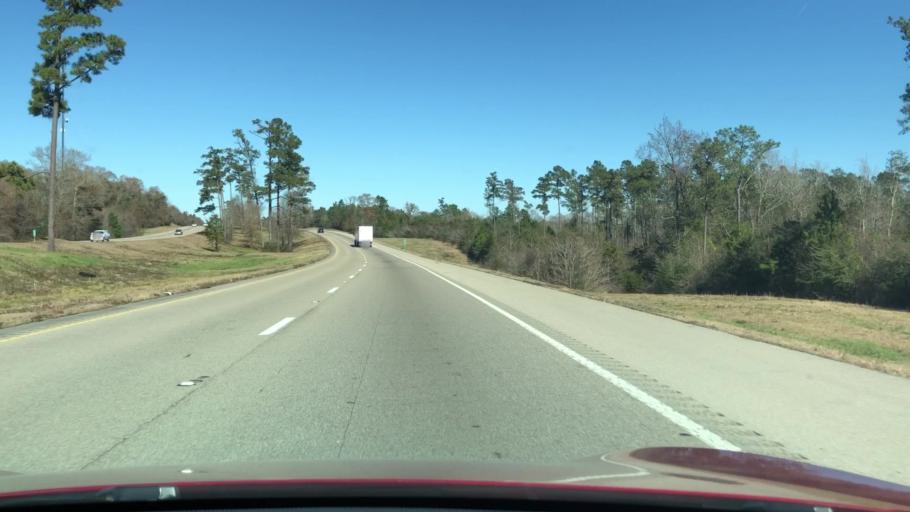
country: US
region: Mississippi
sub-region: Pearl River County
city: Poplarville
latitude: 30.7536
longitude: -89.5220
